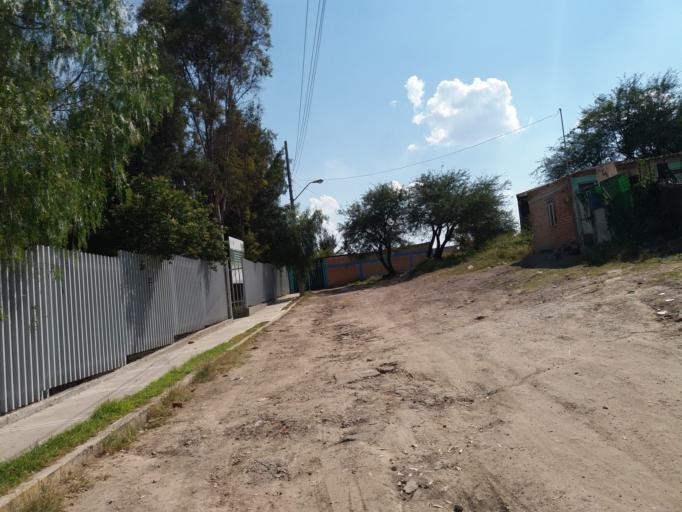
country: MX
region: Aguascalientes
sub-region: Aguascalientes
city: Penuelas (El Cienegal)
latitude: 21.7559
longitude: -102.3005
